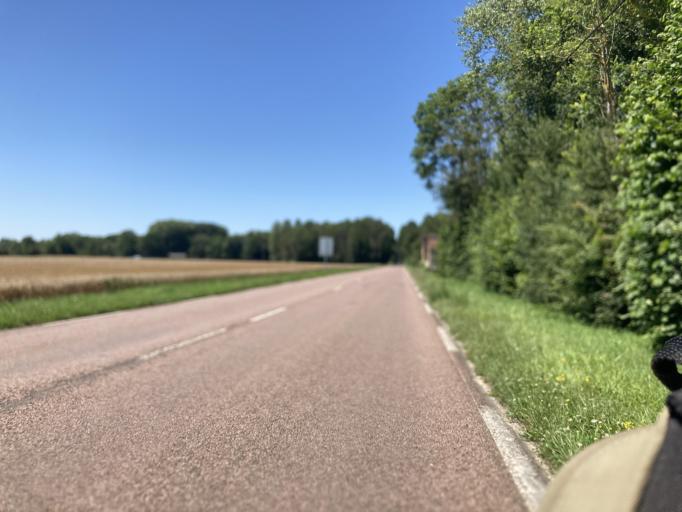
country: FR
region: Bourgogne
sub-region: Departement de l'Yonne
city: Laroche-Saint-Cydroine
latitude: 47.9650
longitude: 3.4695
